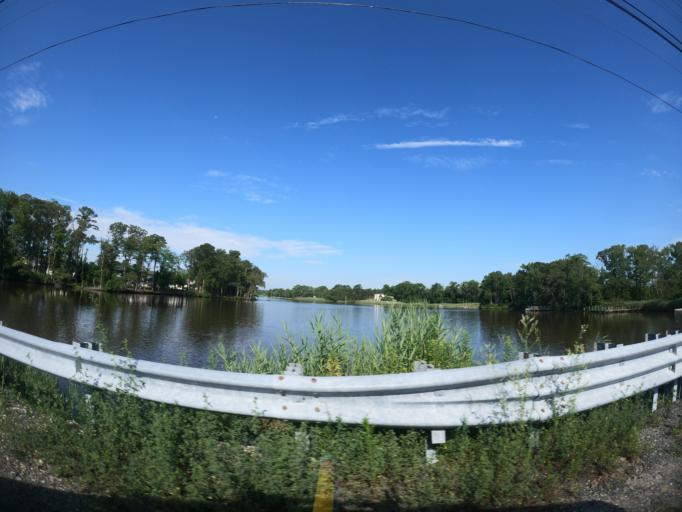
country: US
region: Delaware
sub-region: Sussex County
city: Ocean View
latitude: 38.4834
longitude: -75.1189
